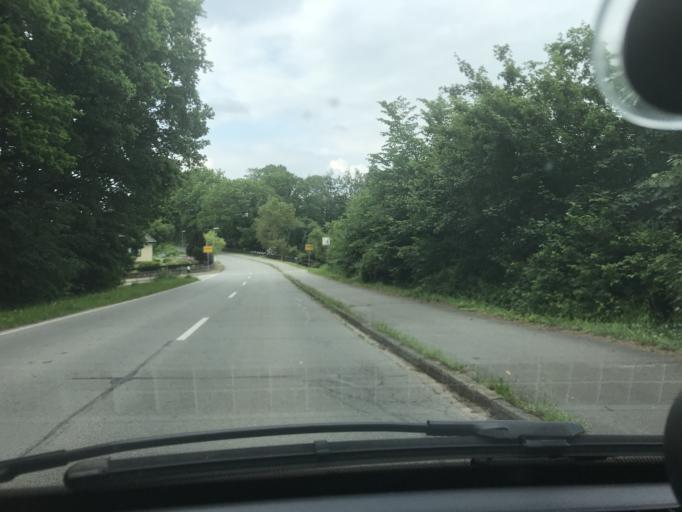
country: DE
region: Schleswig-Holstein
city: Grossensee
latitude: 53.6062
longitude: 10.3352
